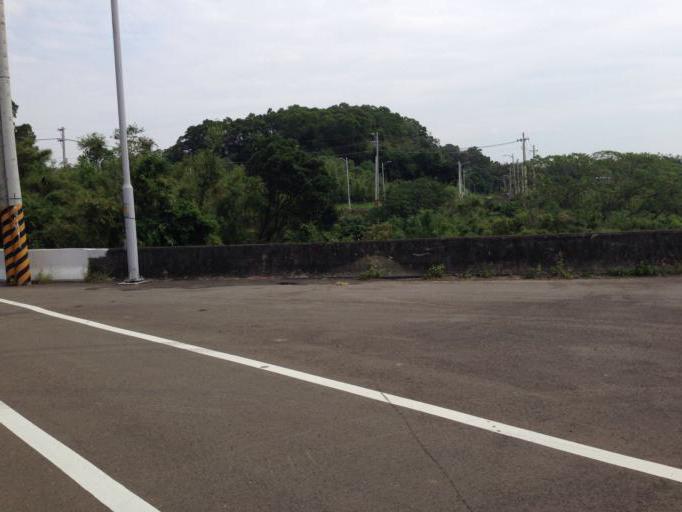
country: TW
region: Taiwan
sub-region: Hsinchu
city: Hsinchu
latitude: 24.7485
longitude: 120.9574
